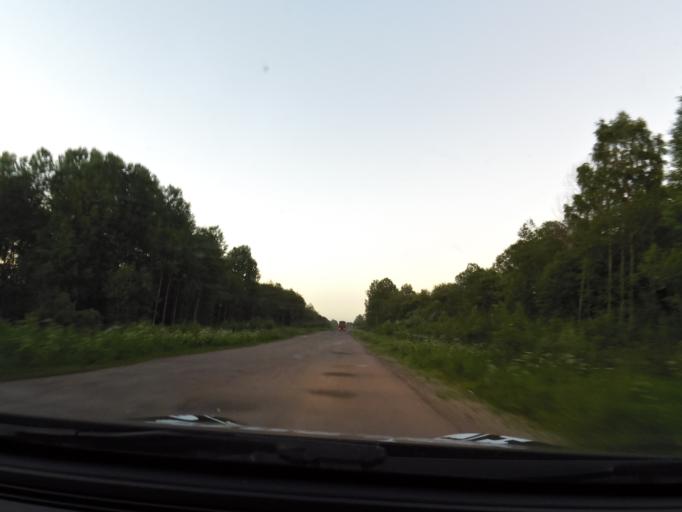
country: RU
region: Vologda
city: Vytegra
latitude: 60.8727
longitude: 36.0217
